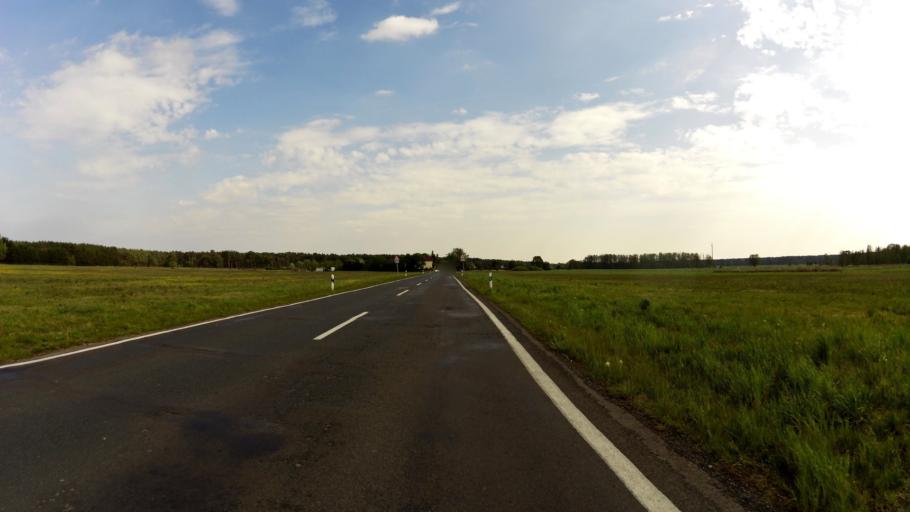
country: DE
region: Brandenburg
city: Spreenhagen
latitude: 52.3384
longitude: 13.8903
